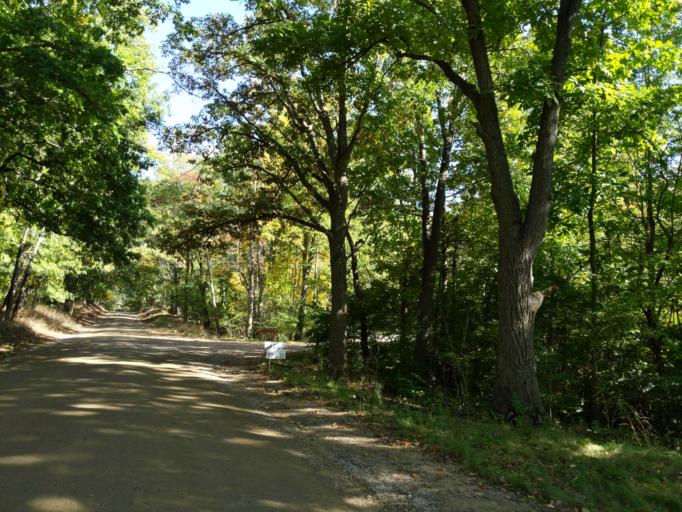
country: US
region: Michigan
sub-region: Clinton County
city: Bath
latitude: 42.8059
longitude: -84.4376
